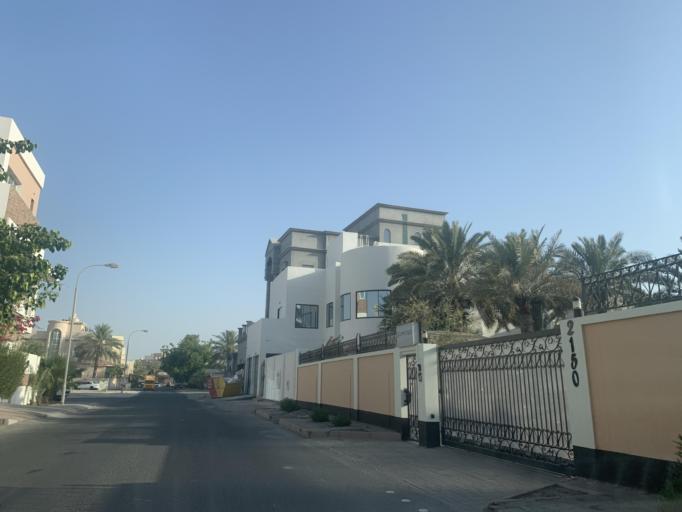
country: BH
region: Manama
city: Jidd Hafs
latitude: 26.2120
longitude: 50.5300
